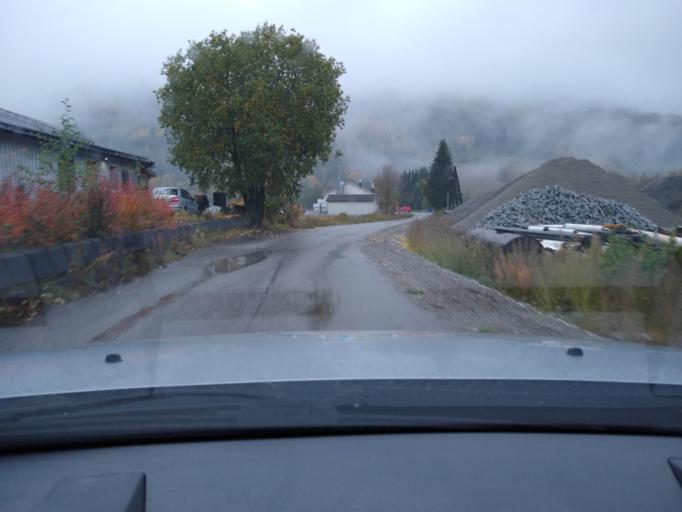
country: NO
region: Oppland
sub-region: Ringebu
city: Ringebu
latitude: 61.5429
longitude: 10.0548
